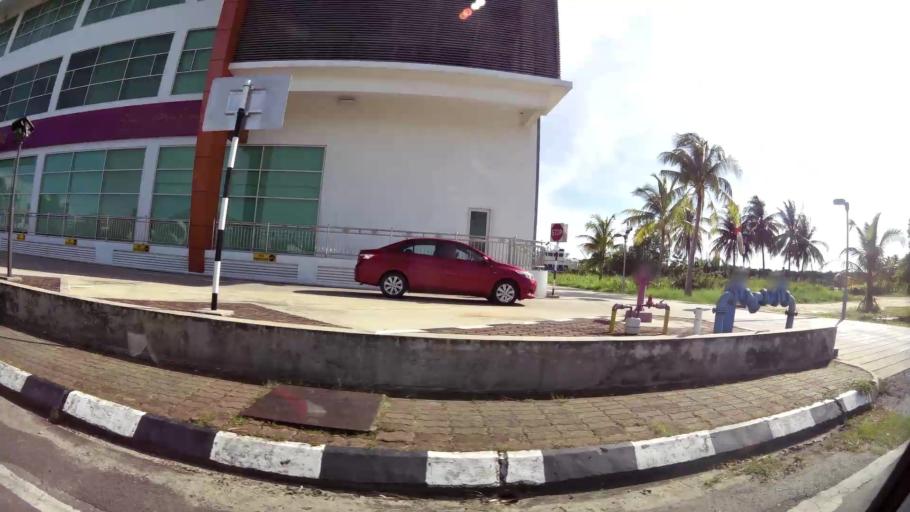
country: BN
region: Belait
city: Kuala Belait
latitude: 4.5787
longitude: 114.1955
